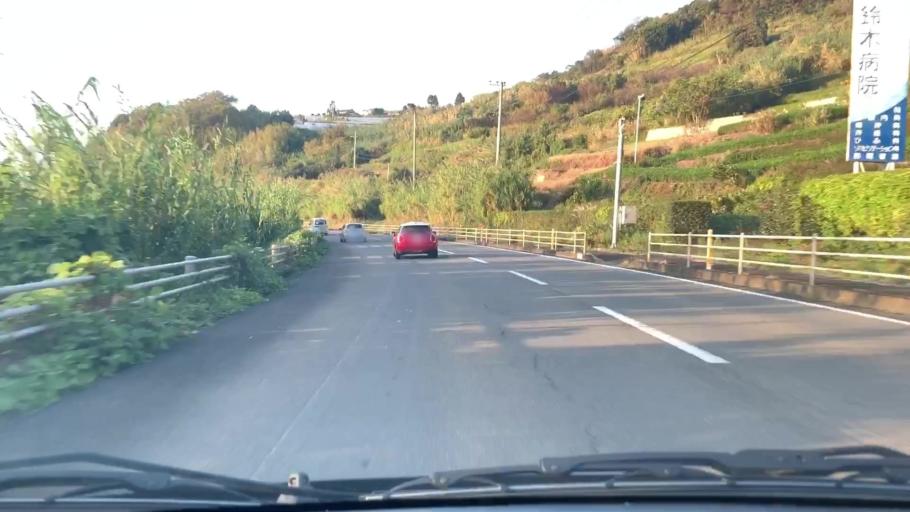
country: JP
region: Nagasaki
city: Omura
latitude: 32.9958
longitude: 129.9487
